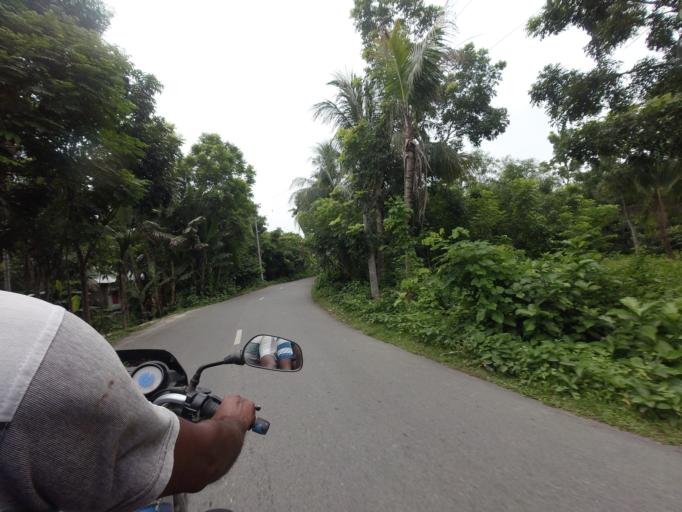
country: BD
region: Khulna
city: Kalia
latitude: 23.1704
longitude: 89.6456
